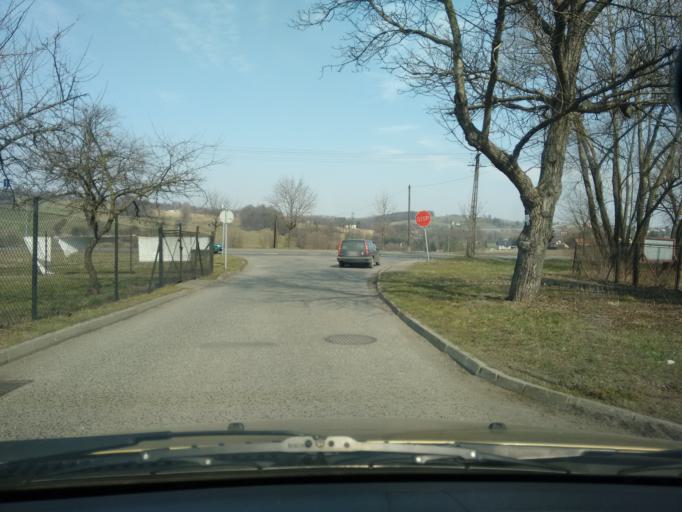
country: PL
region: Silesian Voivodeship
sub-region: Powiat cieszynski
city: Zamarski
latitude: 49.7516
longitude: 18.6671
